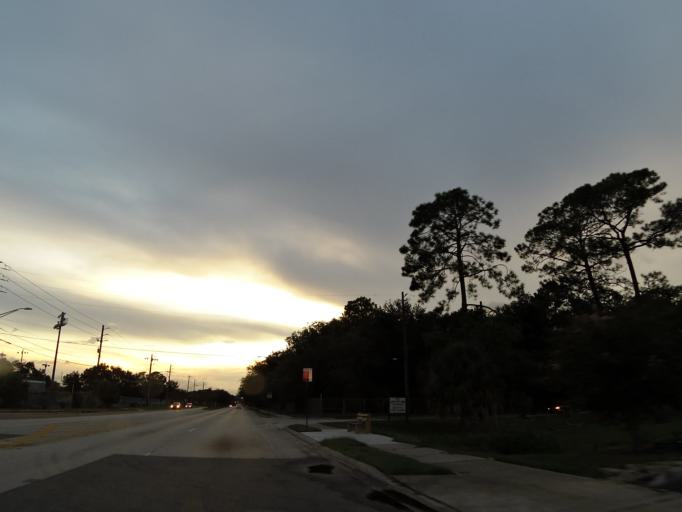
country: US
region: Florida
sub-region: Duval County
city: Jacksonville
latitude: 30.3664
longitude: -81.5897
